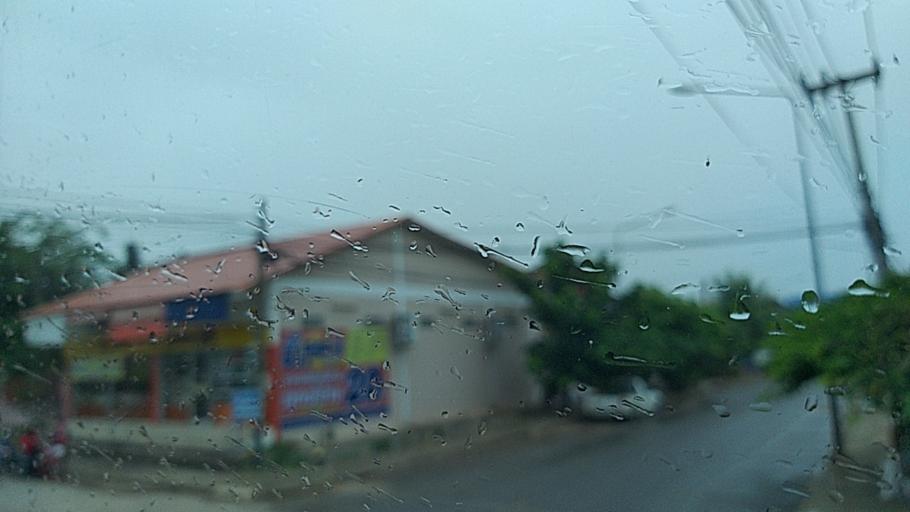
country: TH
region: Maha Sarakham
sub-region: Amphoe Borabue
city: Borabue
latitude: 16.0383
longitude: 103.1219
